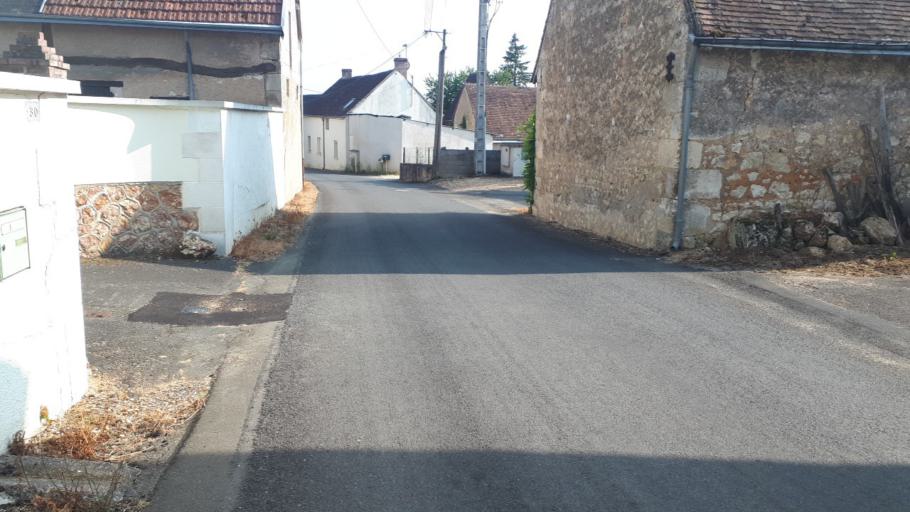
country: FR
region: Centre
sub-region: Departement du Loir-et-Cher
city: Villiers-sur-Loir
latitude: 47.8113
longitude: 0.9927
